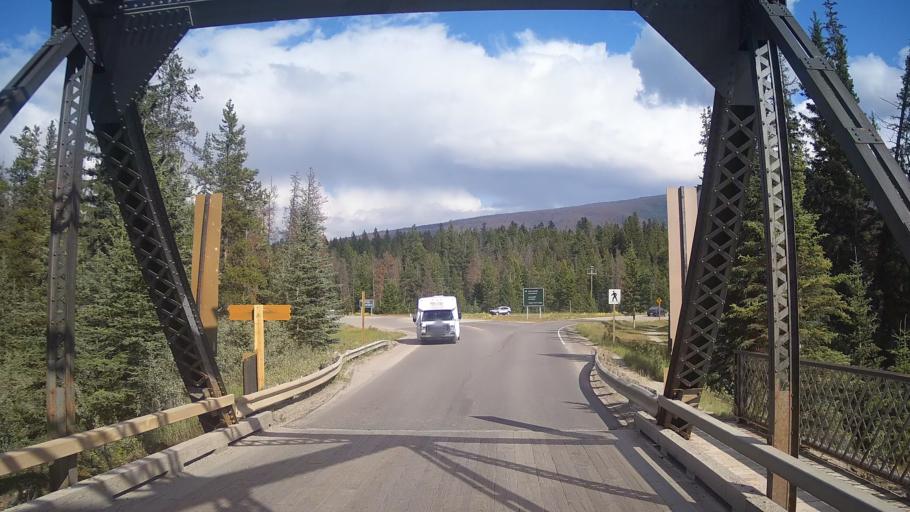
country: CA
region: Alberta
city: Jasper Park Lodge
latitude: 52.9099
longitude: -118.0580
